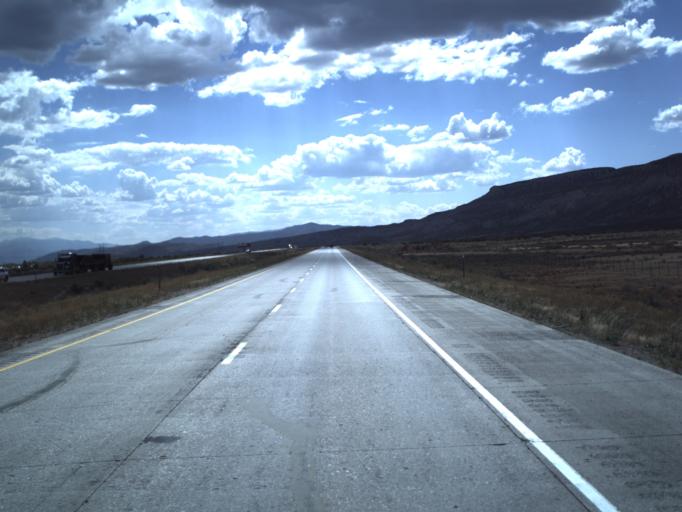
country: US
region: Utah
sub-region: Sevier County
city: Aurora
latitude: 38.8568
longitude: -111.9911
